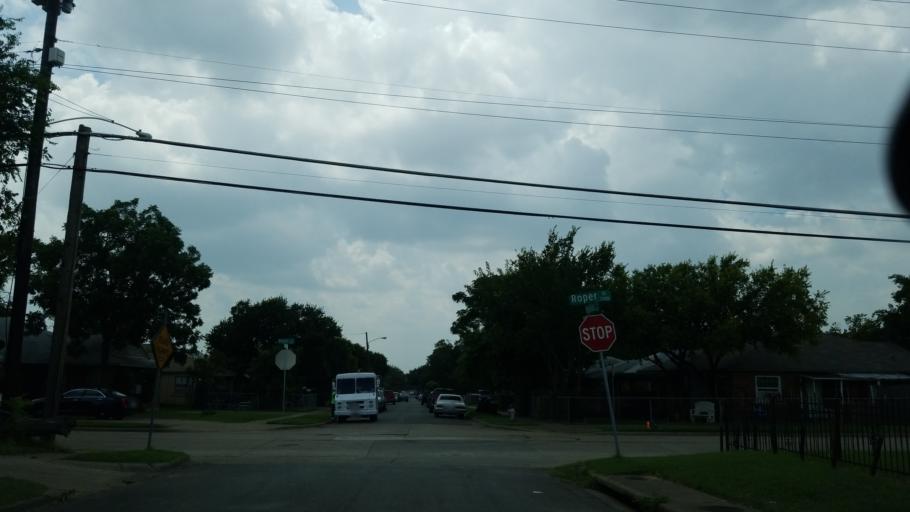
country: US
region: Texas
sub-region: Dallas County
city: University Park
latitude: 32.8477
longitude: -96.8299
